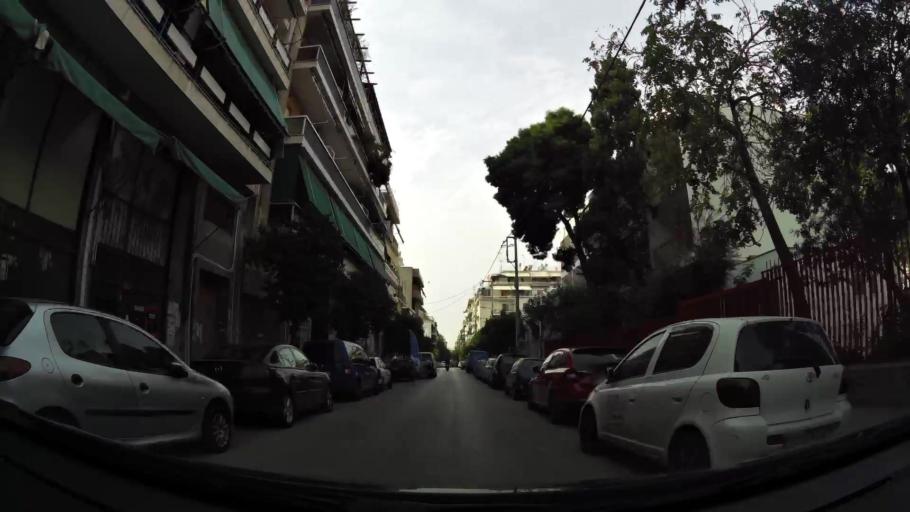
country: GR
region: Attica
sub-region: Nomarchia Athinas
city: Kallithea
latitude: 37.9571
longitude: 23.6985
